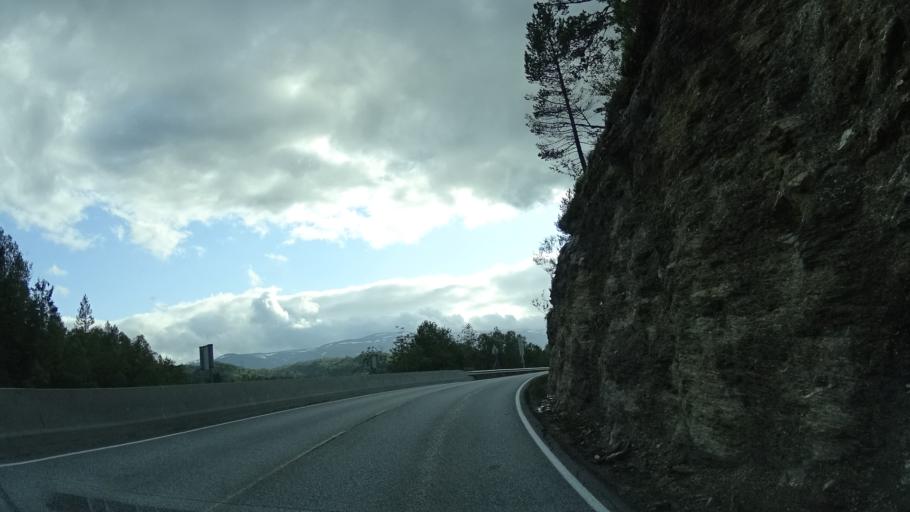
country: NO
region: Hordaland
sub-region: Kvam
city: Norheimsund
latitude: 60.3688
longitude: 6.0314
